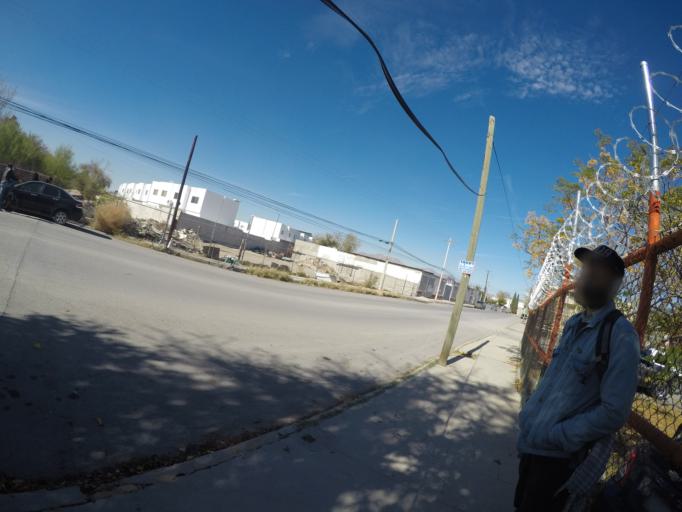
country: MX
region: Chihuahua
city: Ciudad Juarez
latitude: 31.7301
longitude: -106.4276
